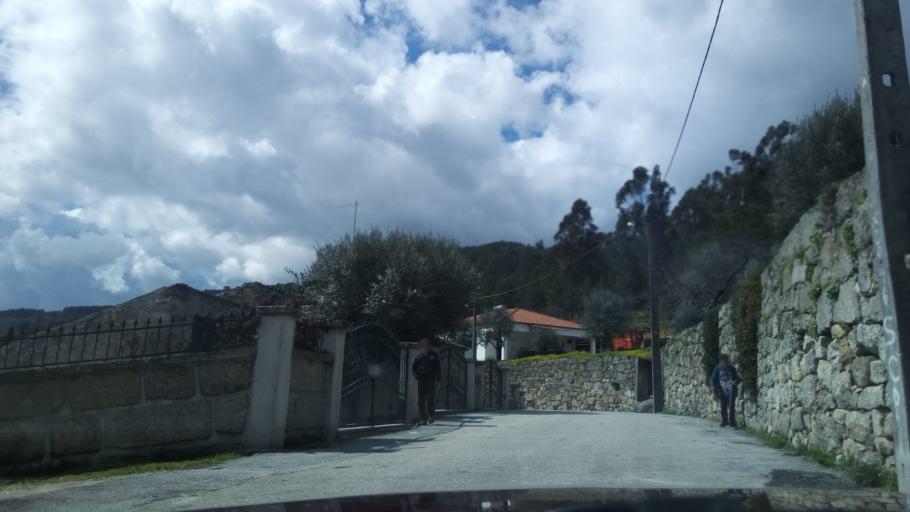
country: PT
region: Guarda
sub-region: Fornos de Algodres
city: Fornos de Algodres
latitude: 40.6625
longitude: -7.4952
